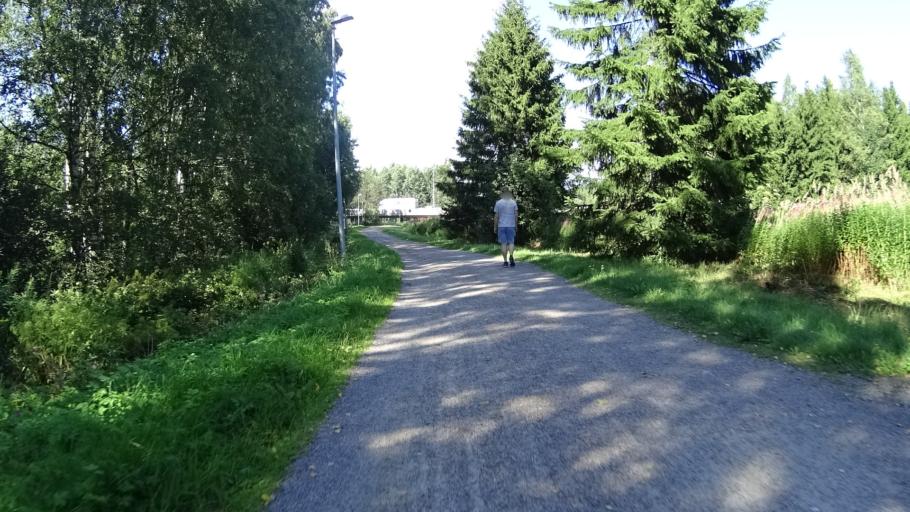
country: FI
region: Uusimaa
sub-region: Helsinki
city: Teekkarikylae
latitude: 60.2334
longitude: 24.8683
